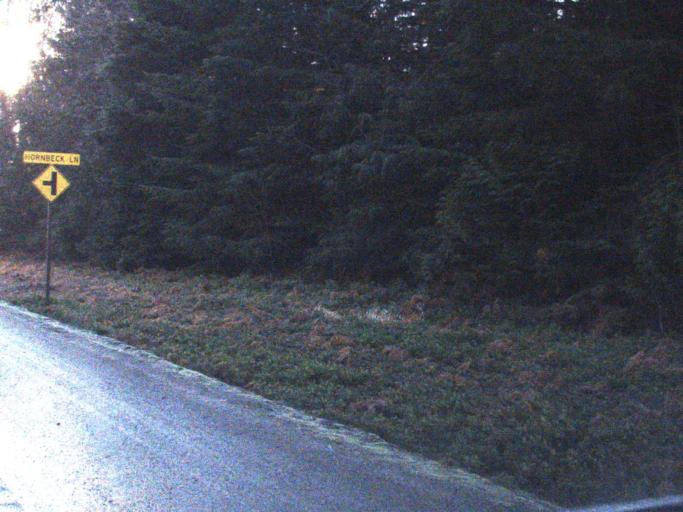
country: US
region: Washington
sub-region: Snohomish County
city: Darrington
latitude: 48.4951
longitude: -121.6417
